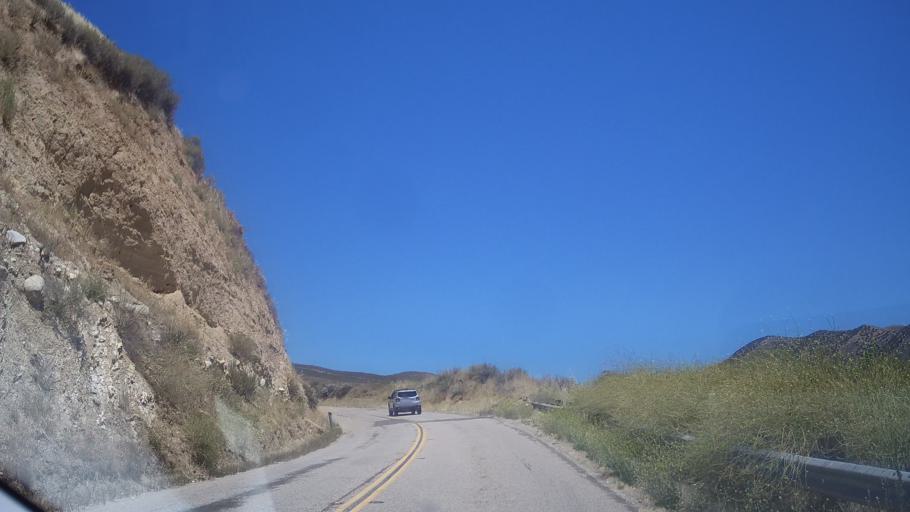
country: US
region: California
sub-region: Monterey County
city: Greenfield
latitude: 36.2696
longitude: -121.3524
